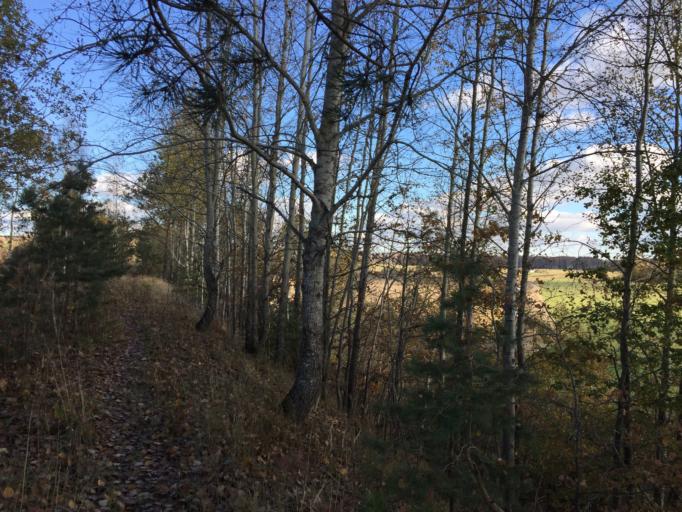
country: LV
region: Tukuma Rajons
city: Tukums
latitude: 56.9578
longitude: 23.0847
